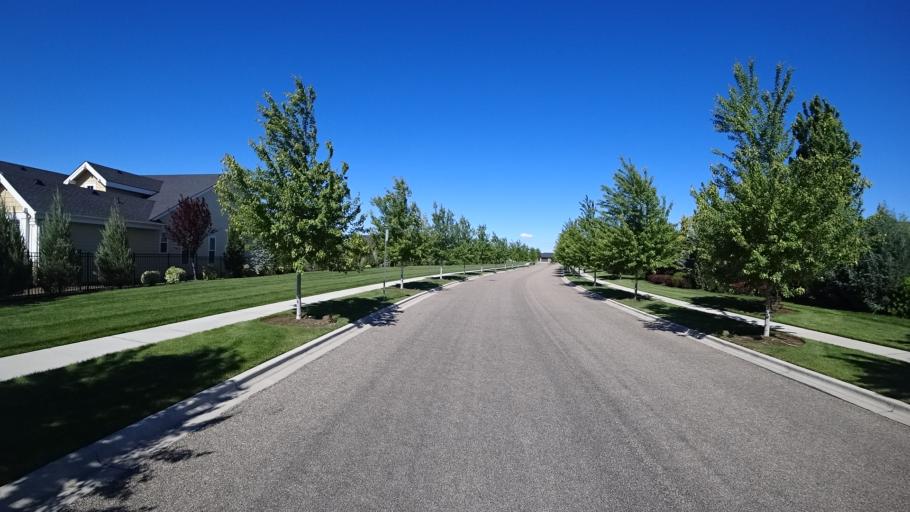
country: US
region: Idaho
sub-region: Ada County
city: Eagle
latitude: 43.6672
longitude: -116.3966
